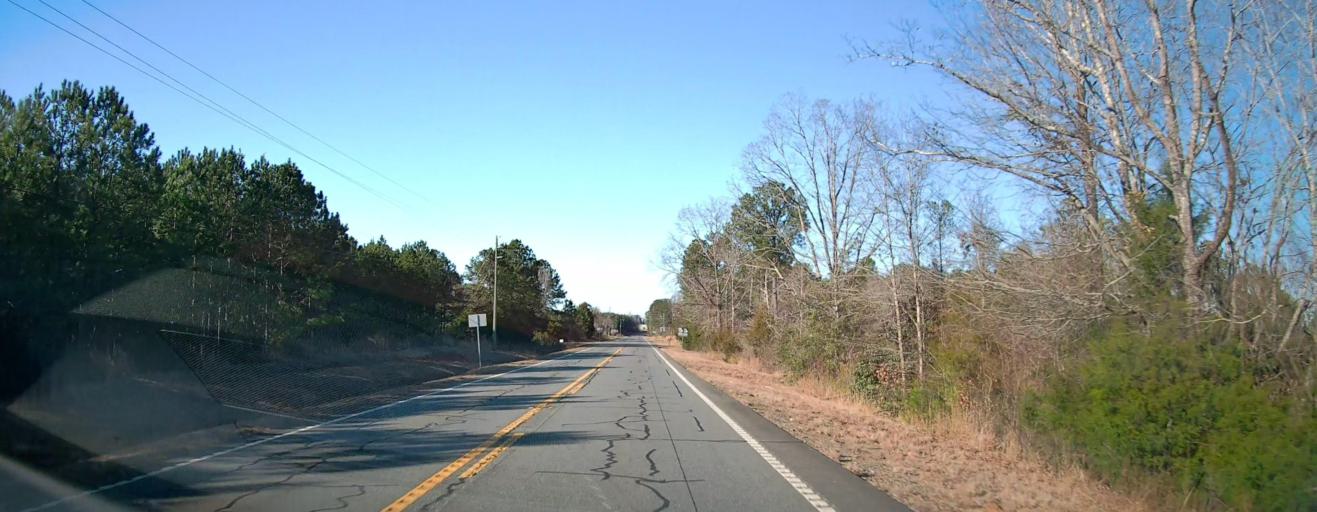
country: US
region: Georgia
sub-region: Talbot County
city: Talbotton
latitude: 32.7604
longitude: -84.5579
